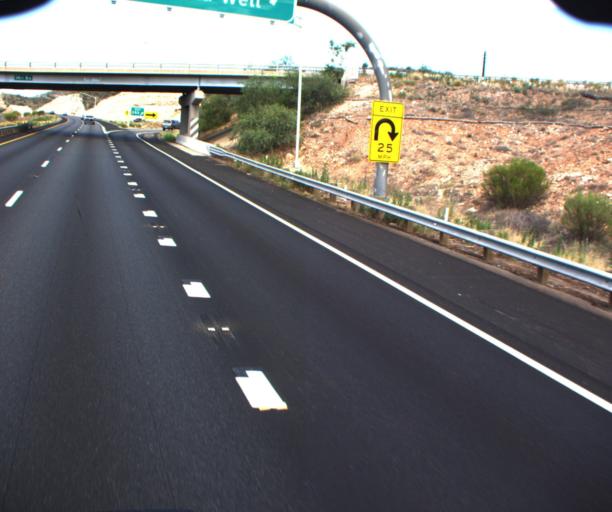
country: US
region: Arizona
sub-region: Yavapai County
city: Lake Montezuma
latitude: 34.6390
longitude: -111.8164
